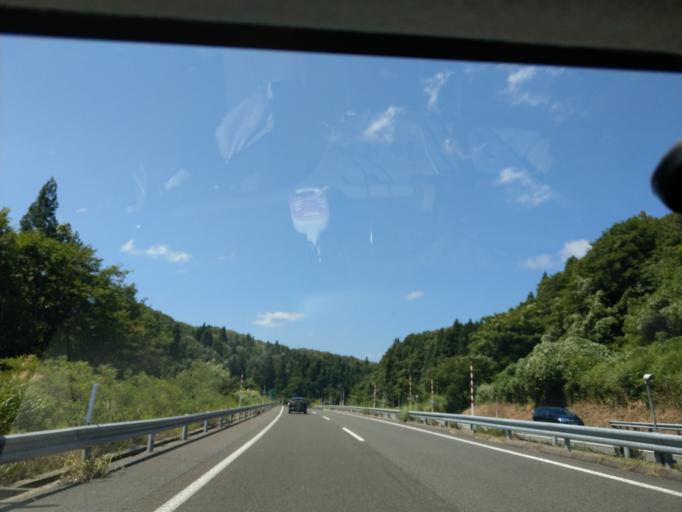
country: JP
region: Akita
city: Akita
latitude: 39.5798
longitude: 140.2928
